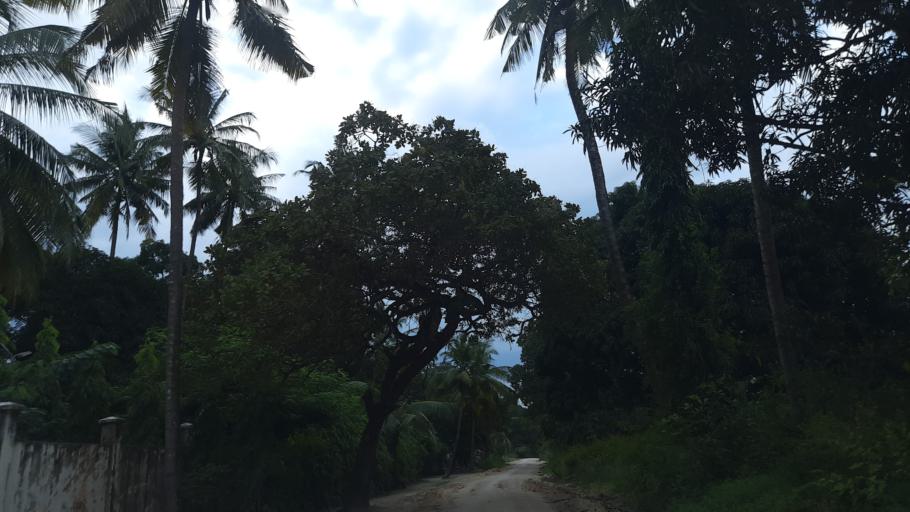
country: TZ
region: Pwani
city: Bagamoyo
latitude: -6.5161
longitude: 38.9292
